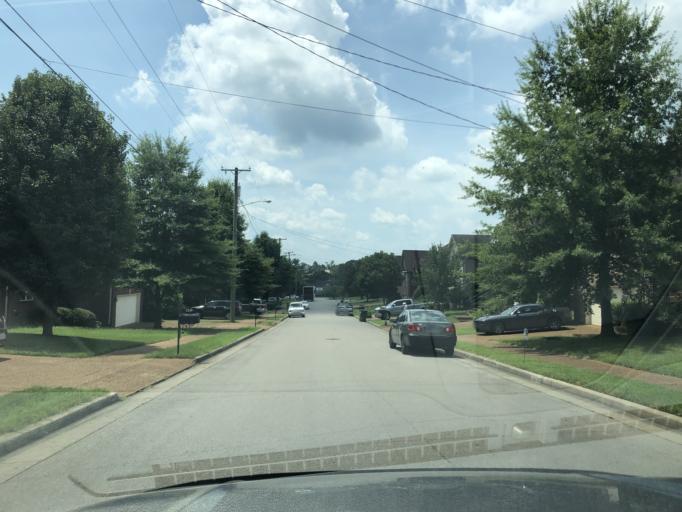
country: US
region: Tennessee
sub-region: Williamson County
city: Nolensville
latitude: 36.0158
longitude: -86.6939
